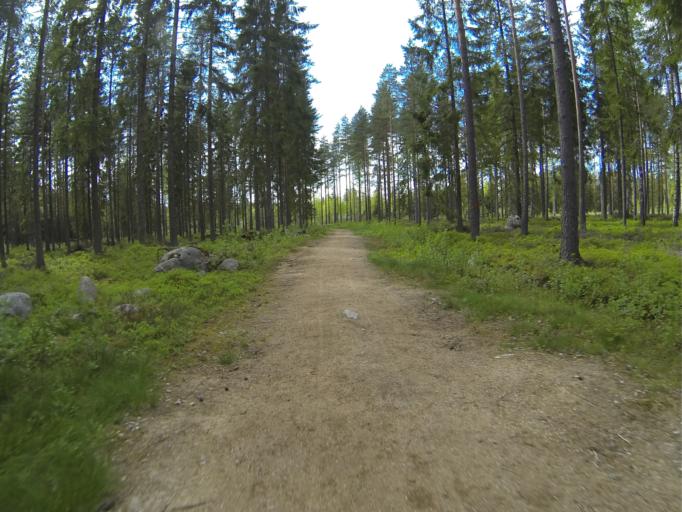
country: FI
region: Varsinais-Suomi
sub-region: Salo
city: Salo
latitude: 60.3901
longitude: 23.1915
